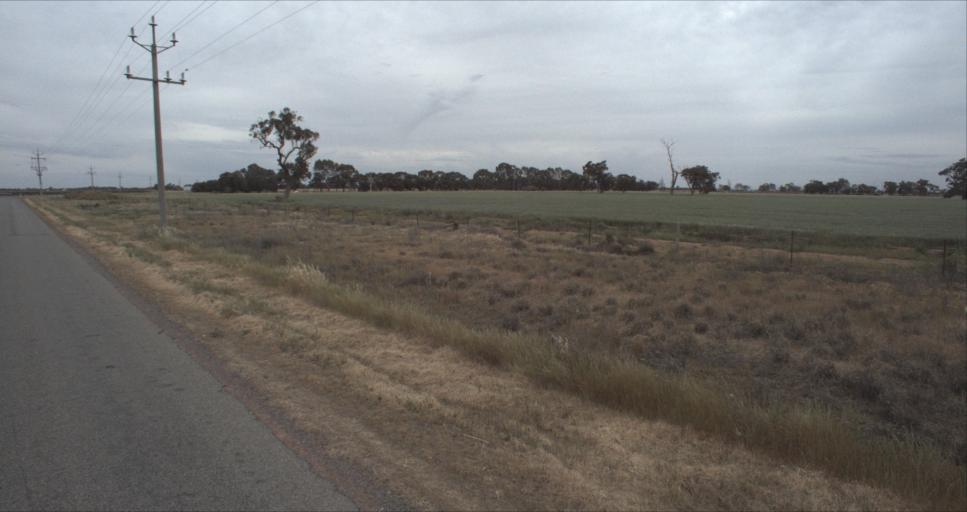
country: AU
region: New South Wales
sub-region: Leeton
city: Leeton
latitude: -34.4988
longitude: 146.4000
